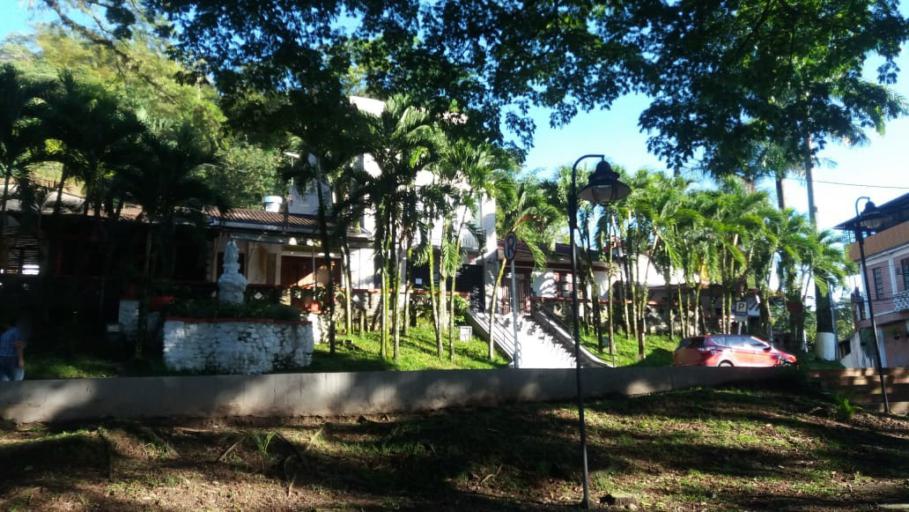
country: CO
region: Meta
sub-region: Villavicencio
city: Villavicencio
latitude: 4.1545
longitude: -73.6393
